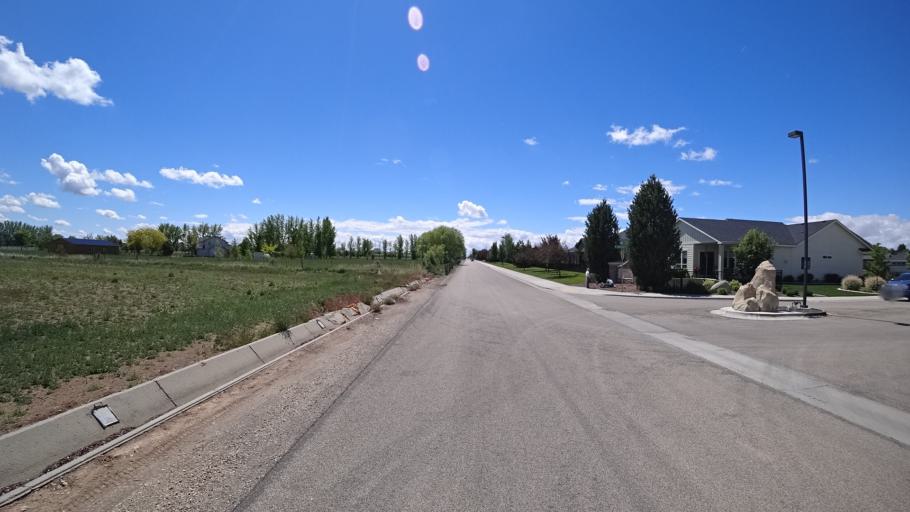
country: US
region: Idaho
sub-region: Ada County
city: Kuna
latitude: 43.5069
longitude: -116.4238
